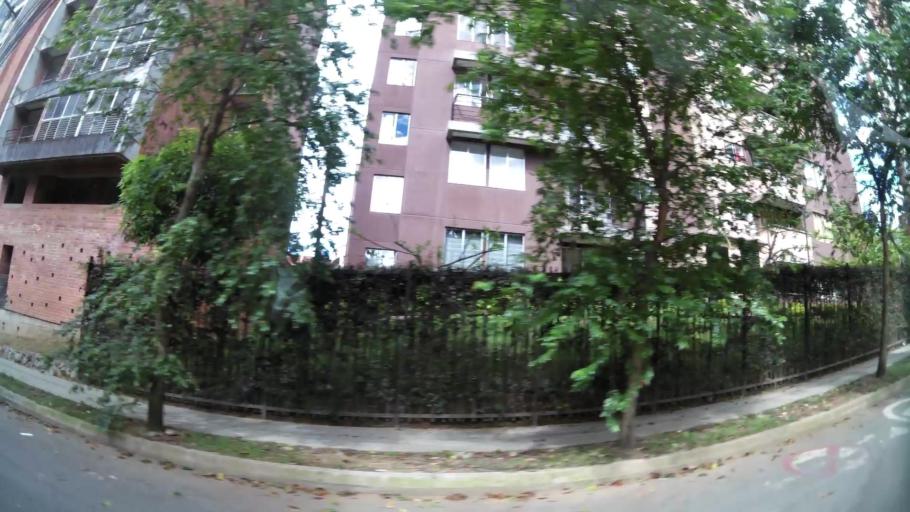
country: CO
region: Antioquia
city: Sabaneta
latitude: 6.1515
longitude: -75.6113
